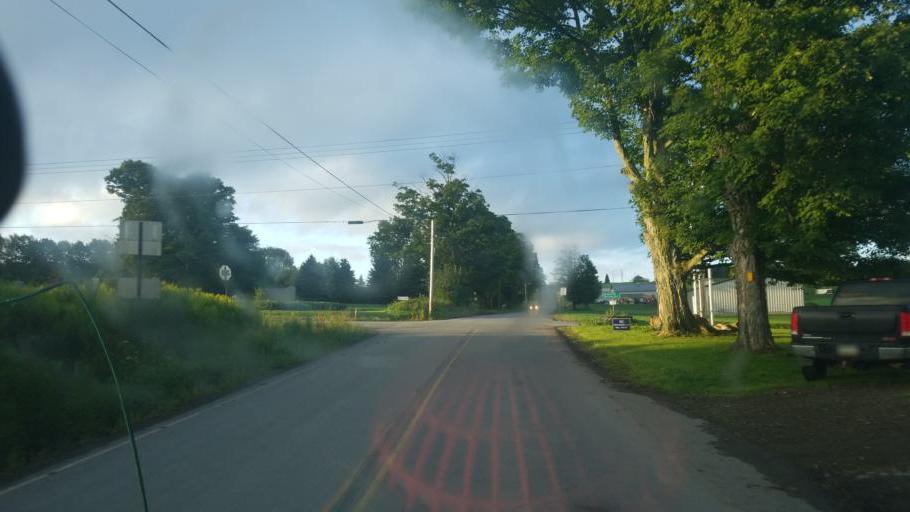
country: US
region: Pennsylvania
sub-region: Potter County
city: Galeton
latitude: 41.8870
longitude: -77.7613
